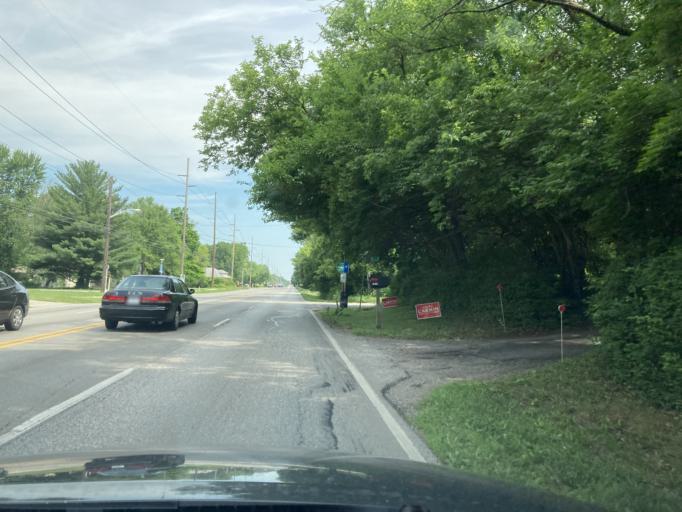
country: US
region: Indiana
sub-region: Marion County
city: Broad Ripple
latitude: 39.8456
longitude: -86.1907
